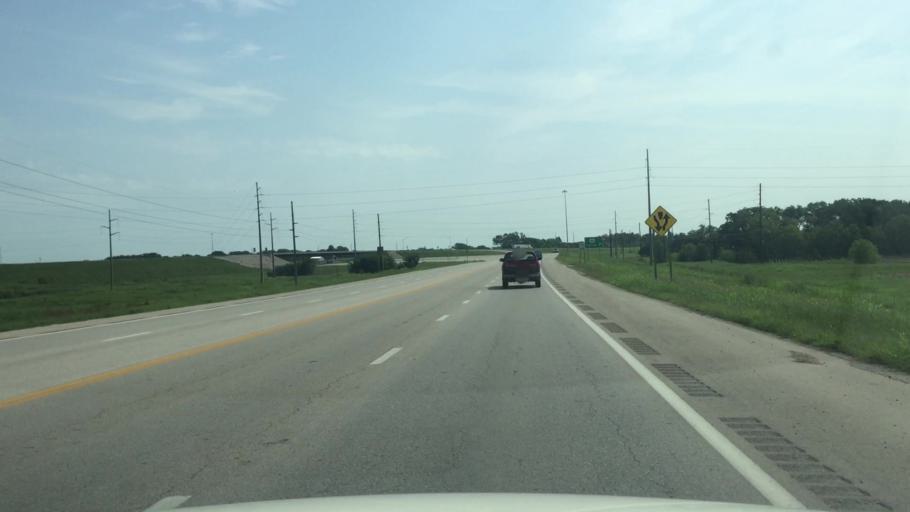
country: US
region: Kansas
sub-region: Montgomery County
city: Coffeyville
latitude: 37.0428
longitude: -95.5888
